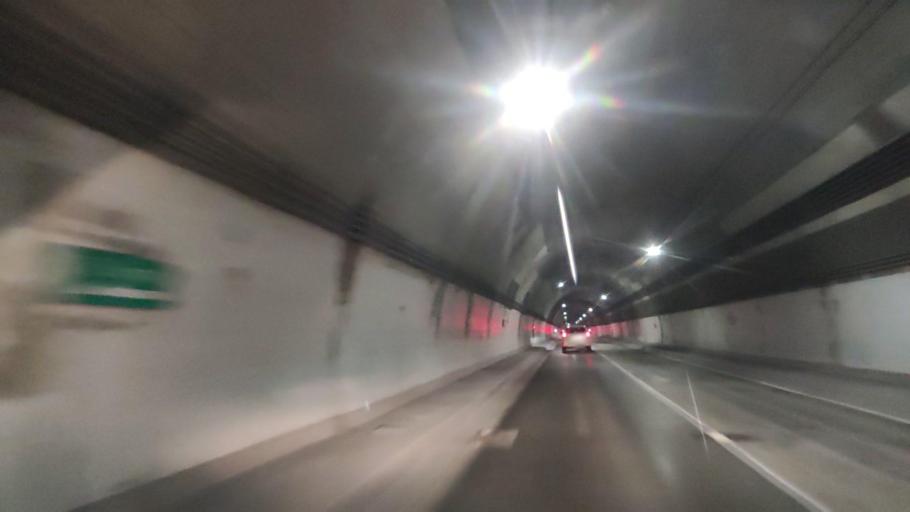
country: JP
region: Hokkaido
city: Ishikari
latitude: 43.4466
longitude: 141.4116
